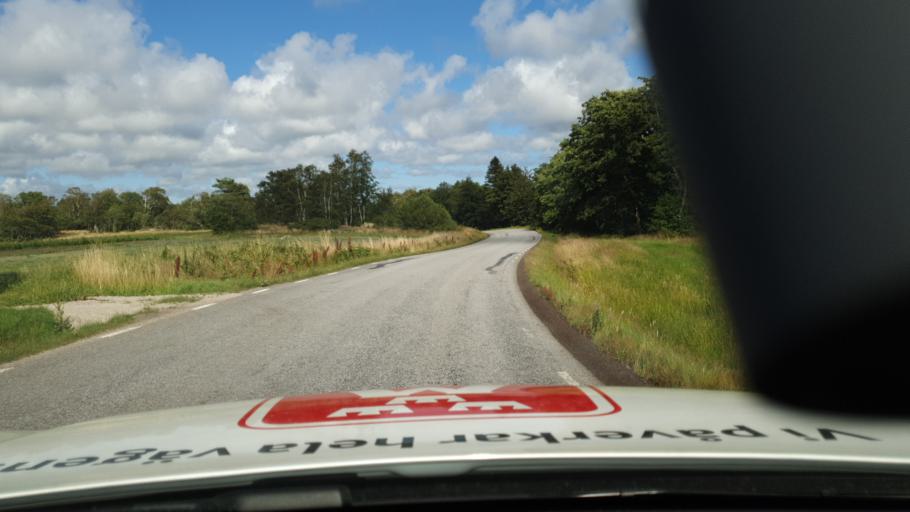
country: SE
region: Vaestra Goetaland
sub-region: Lysekils Kommun
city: Lysekil
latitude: 58.1846
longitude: 11.4909
